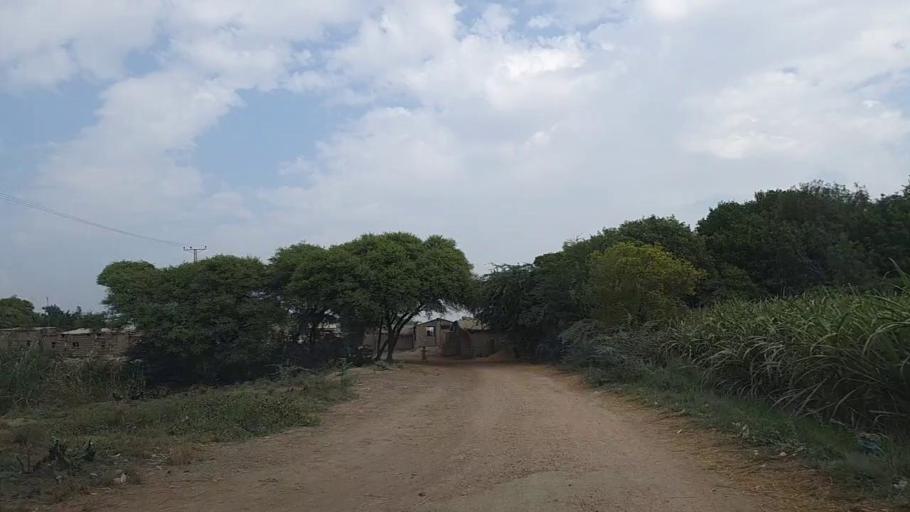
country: PK
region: Sindh
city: Daro Mehar
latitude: 24.7162
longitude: 68.1586
